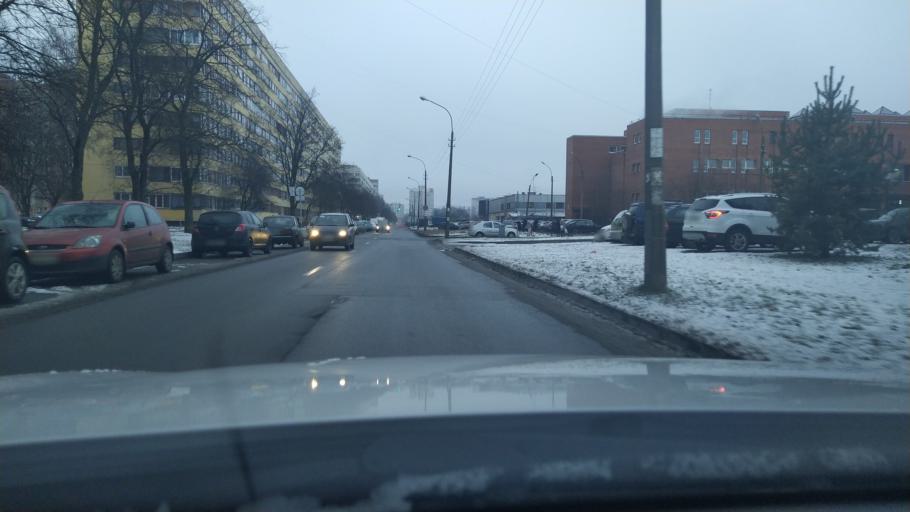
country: RU
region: St.-Petersburg
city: Grazhdanka
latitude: 60.0436
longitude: 30.3934
